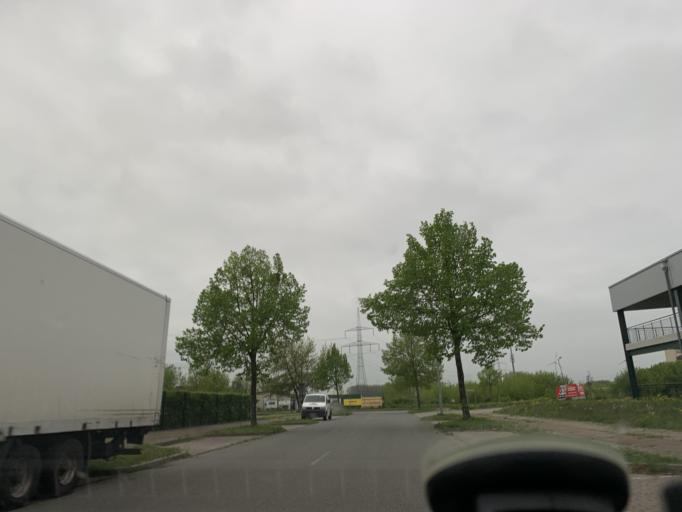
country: DE
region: Brandenburg
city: Nauen
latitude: 52.5962
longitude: 12.8909
